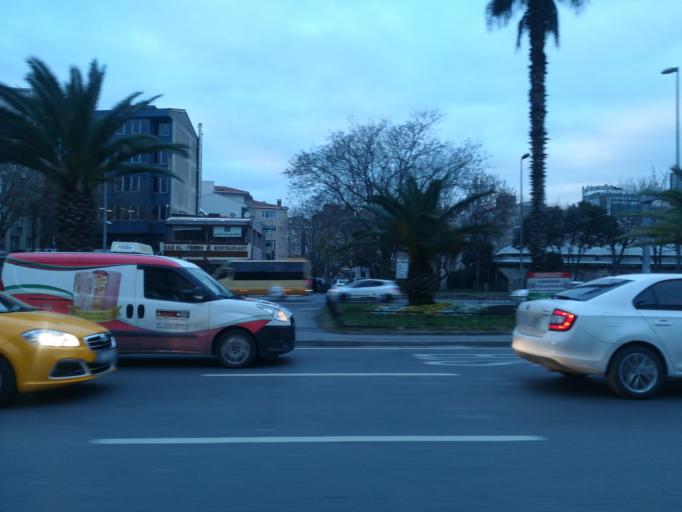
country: TR
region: Istanbul
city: Istanbul
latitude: 41.0154
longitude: 28.9428
